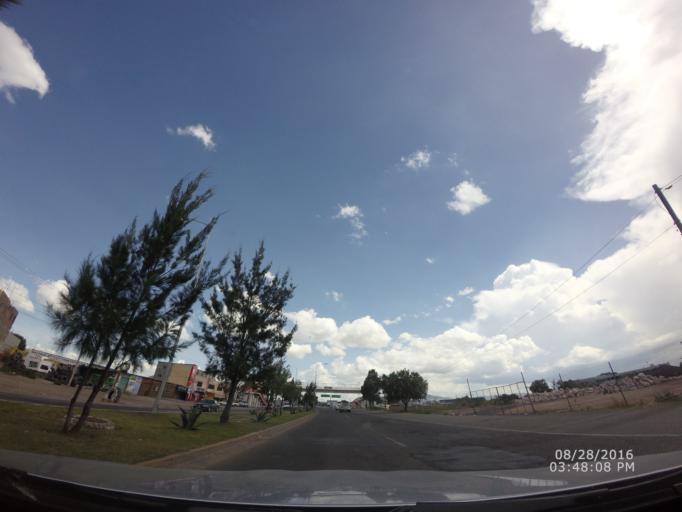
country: MX
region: Hidalgo
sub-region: Mineral de la Reforma
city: Nuevo Centro de Poblacion Agricola el Chacon
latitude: 20.0596
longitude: -98.7436
